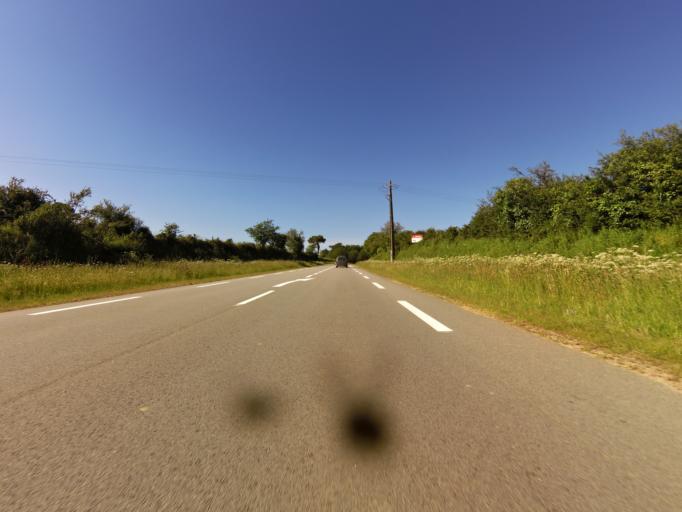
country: FR
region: Brittany
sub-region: Departement du Morbihan
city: Ferel
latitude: 47.5069
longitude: -2.3779
